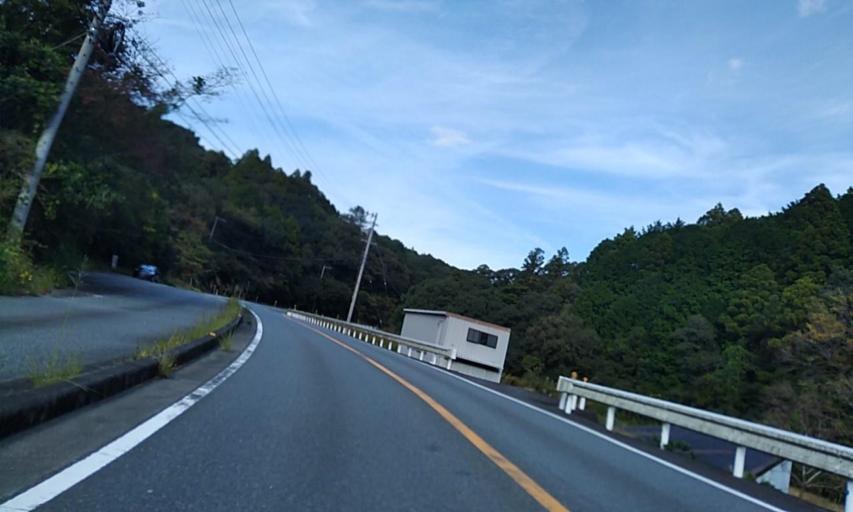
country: JP
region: Mie
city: Ise
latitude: 34.3540
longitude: 136.7413
